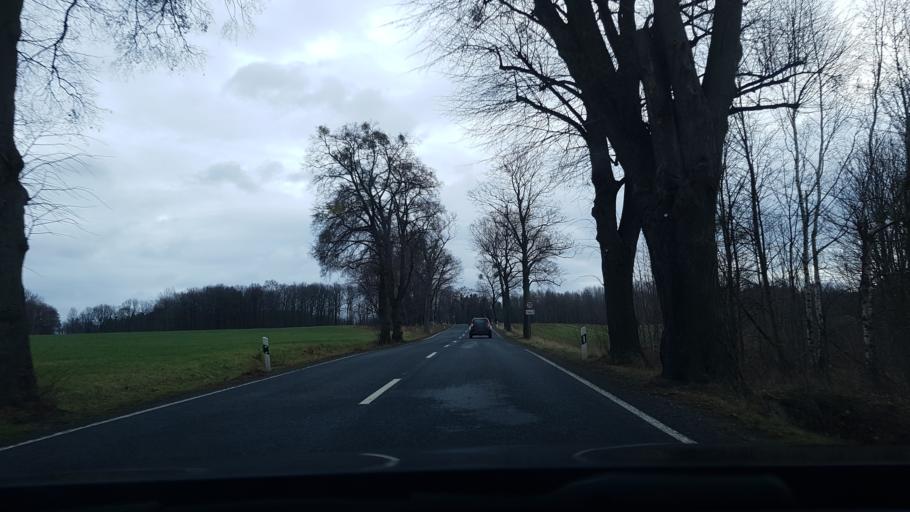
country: DE
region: Saxony
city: Dohma
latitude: 50.8957
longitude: 13.9461
